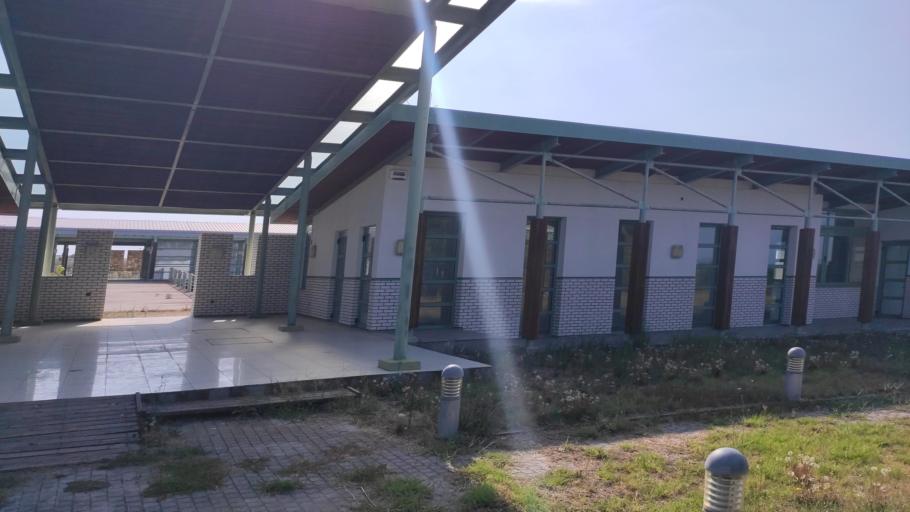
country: GR
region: Central Macedonia
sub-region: Nomos Pellis
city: Pella
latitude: 40.7515
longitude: 22.5176
